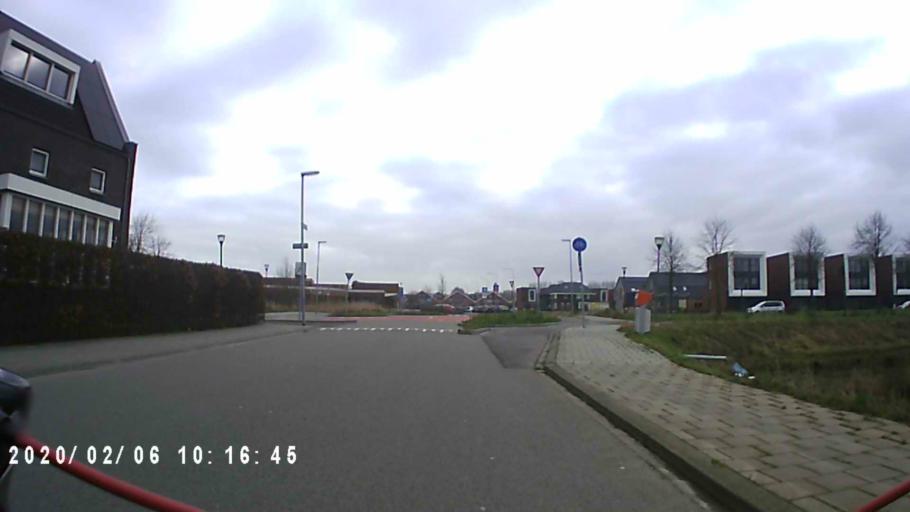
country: NL
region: Groningen
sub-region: Gemeente Groningen
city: Korrewegwijk
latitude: 53.2384
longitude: 6.5183
